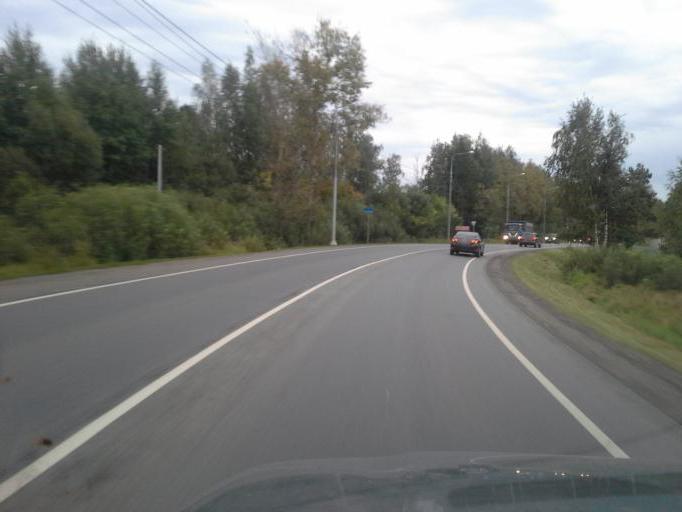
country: RU
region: Moskovskaya
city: Zhavoronki
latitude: 55.6656
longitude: 37.0925
